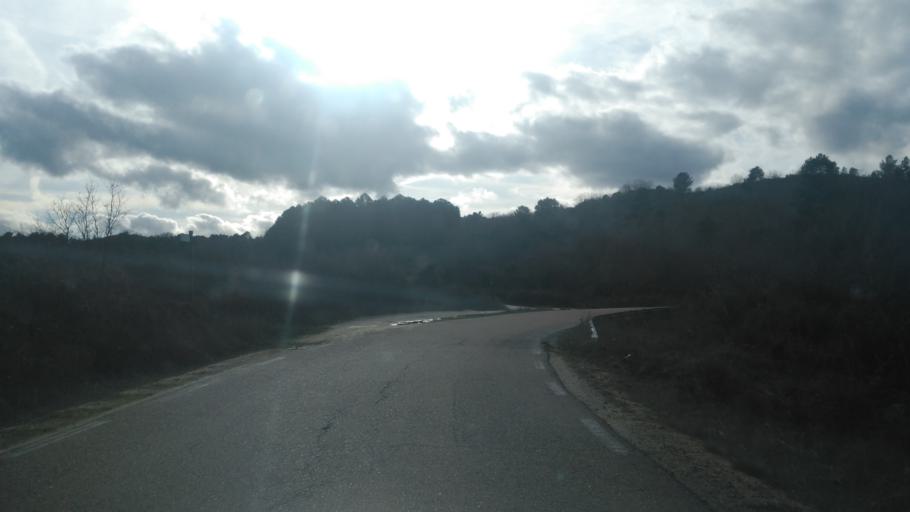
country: ES
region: Castille and Leon
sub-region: Provincia de Salamanca
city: Villanueva del Conde
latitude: 40.4897
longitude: -6.0185
